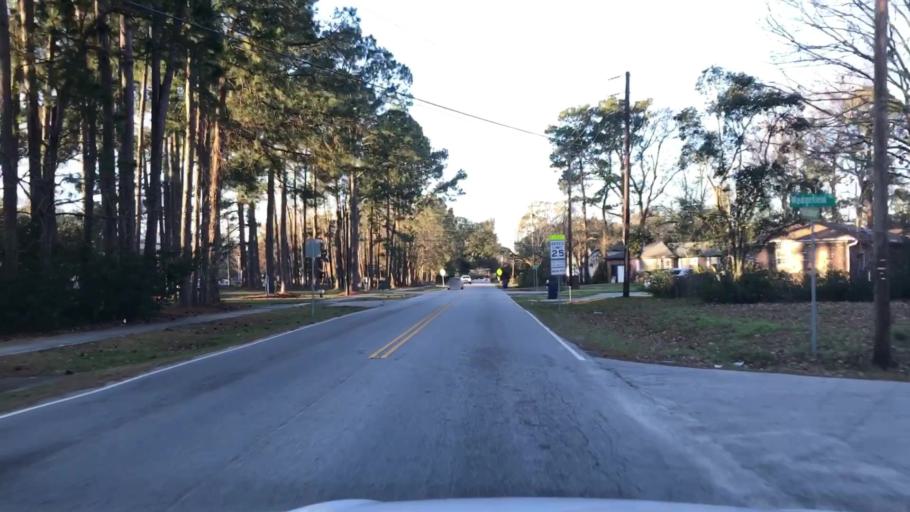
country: US
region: South Carolina
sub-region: Charleston County
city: North Charleston
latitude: 32.8142
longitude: -80.0176
